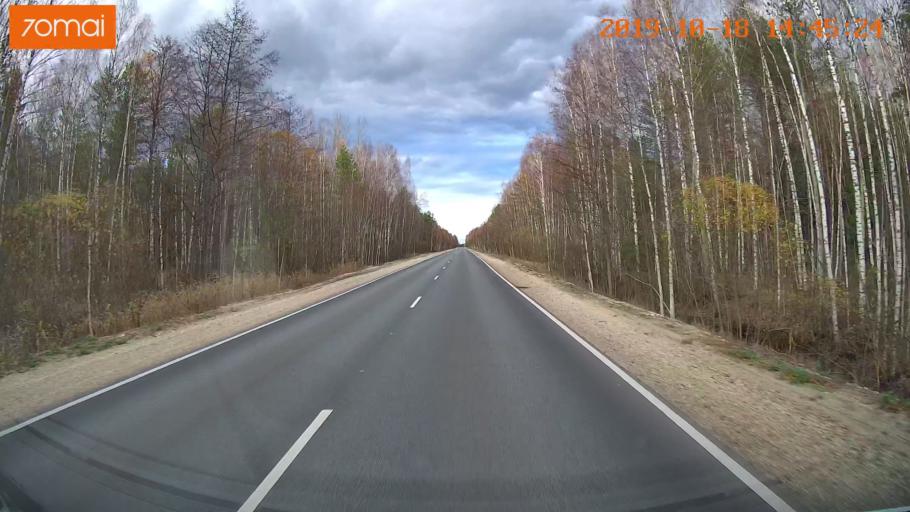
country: RU
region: Vladimir
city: Velikodvorskiy
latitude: 55.3544
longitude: 40.6788
